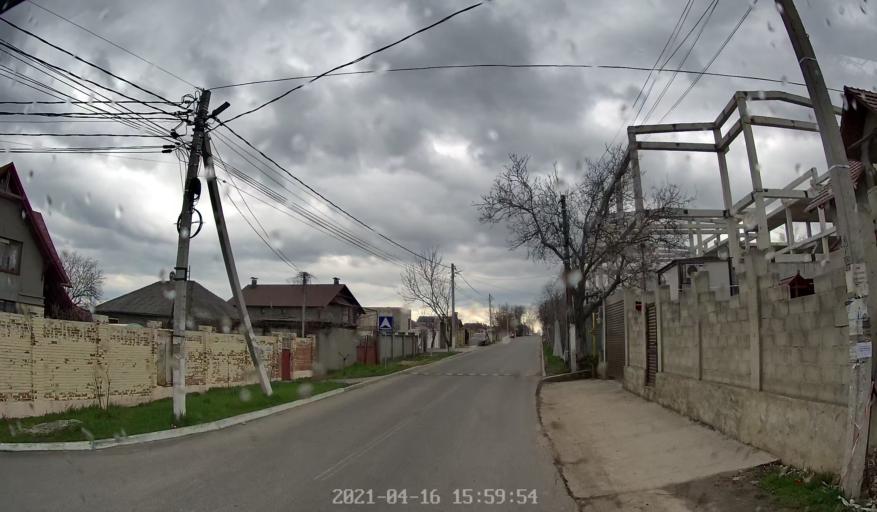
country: MD
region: Chisinau
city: Stauceni
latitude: 47.0961
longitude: 28.8641
